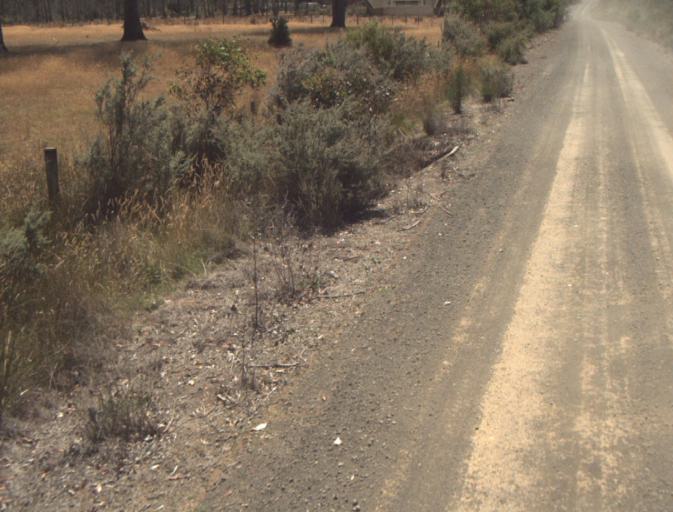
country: AU
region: Tasmania
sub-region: Launceston
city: Mayfield
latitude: -41.2747
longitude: 147.0990
